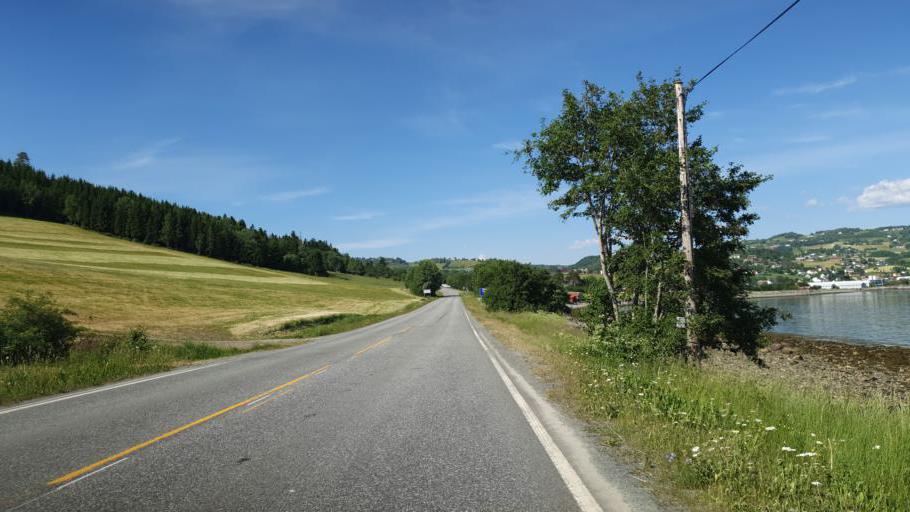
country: NO
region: Nord-Trondelag
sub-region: Leksvik
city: Leksvik
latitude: 63.6604
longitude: 10.6084
